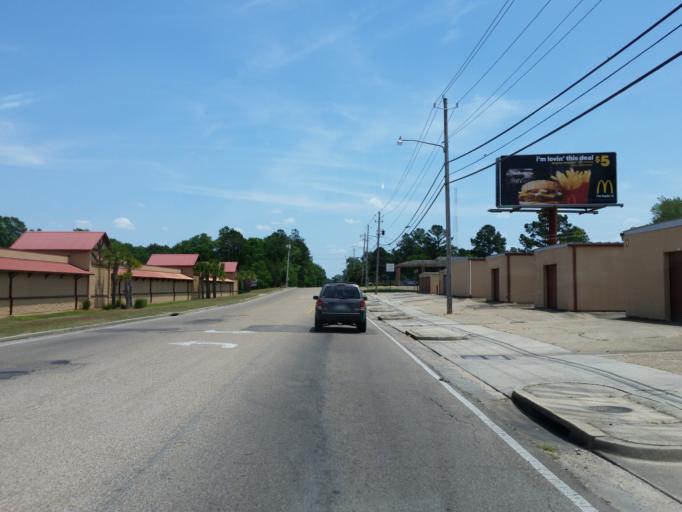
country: US
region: Mississippi
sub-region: Forrest County
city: Hattiesburg
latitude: 31.3041
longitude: -89.3288
